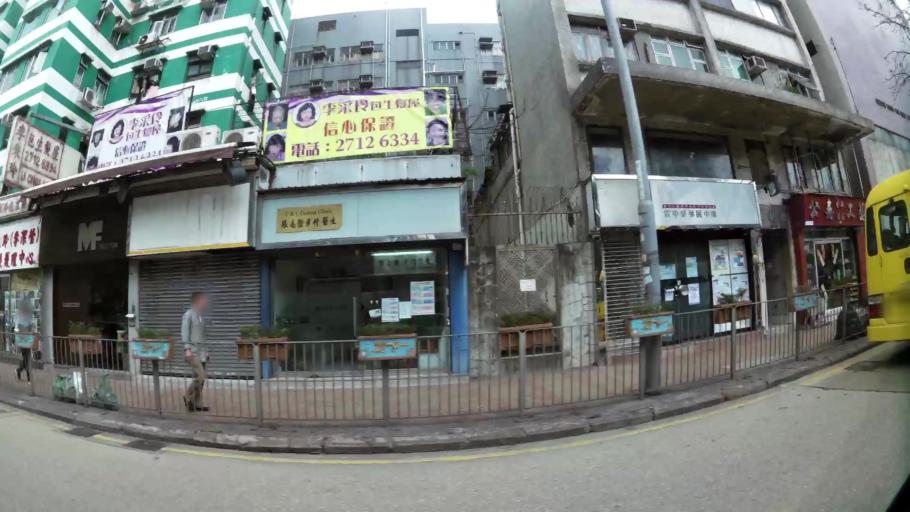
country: HK
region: Kowloon City
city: Kowloon
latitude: 22.3251
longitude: 114.1890
